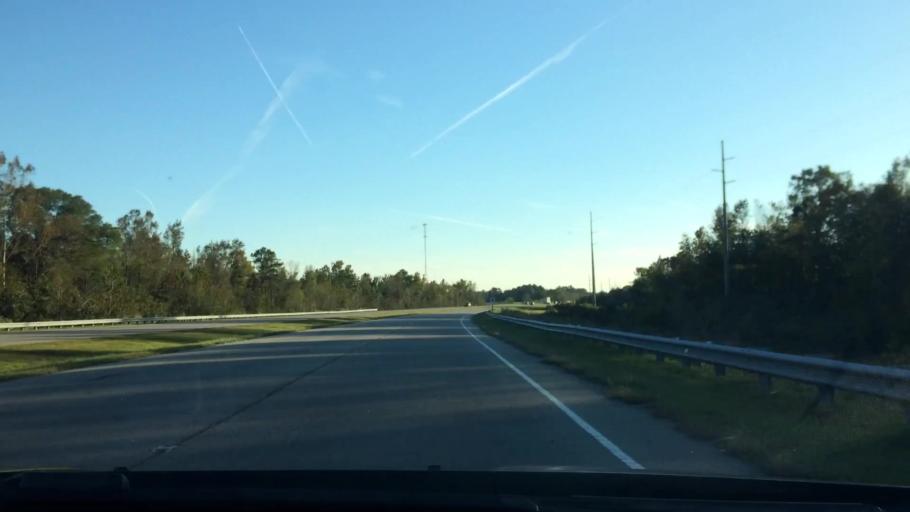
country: US
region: North Carolina
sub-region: Pitt County
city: Grifton
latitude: 35.3801
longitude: -77.4504
